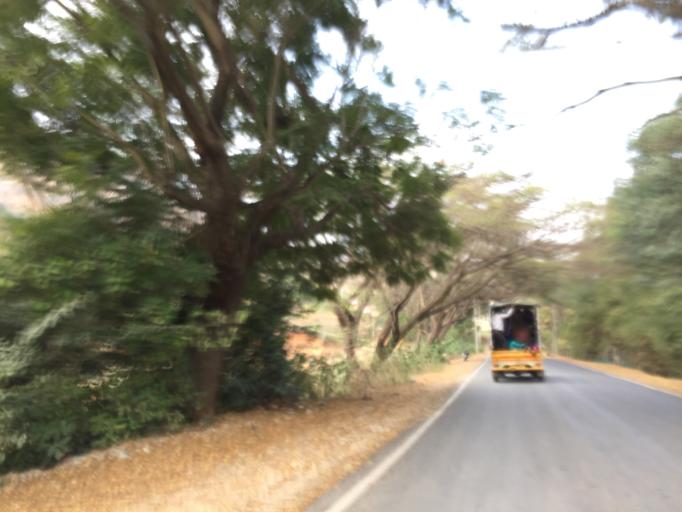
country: IN
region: Karnataka
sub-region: Chikkaballapur
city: Chik Ballapur
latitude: 13.3788
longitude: 77.6744
